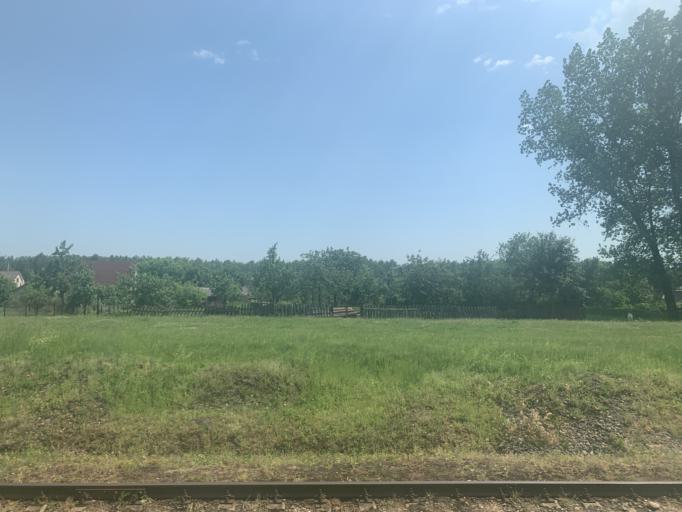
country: BY
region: Minsk
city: Stowbtsy
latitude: 53.4936
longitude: 26.7728
